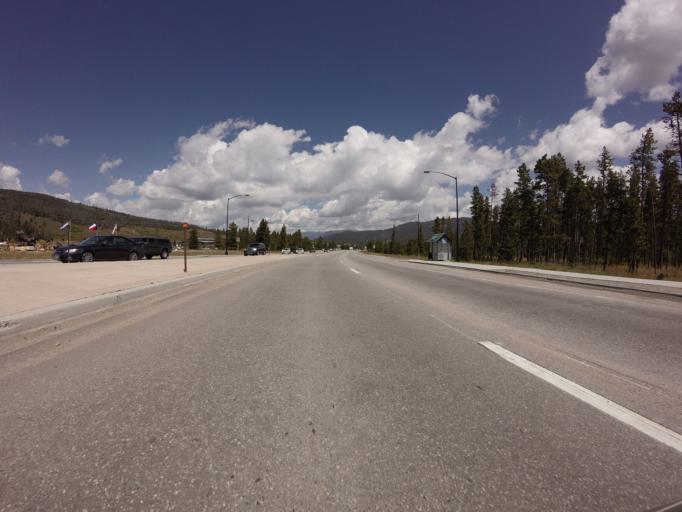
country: US
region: Colorado
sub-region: Summit County
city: Breckenridge
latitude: 39.5262
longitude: -106.0452
